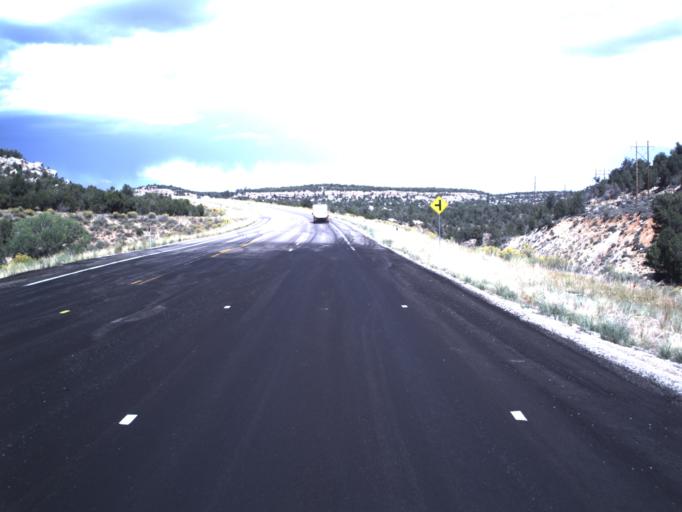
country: US
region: Utah
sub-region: San Juan County
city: Blanding
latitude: 37.6679
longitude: -109.4317
